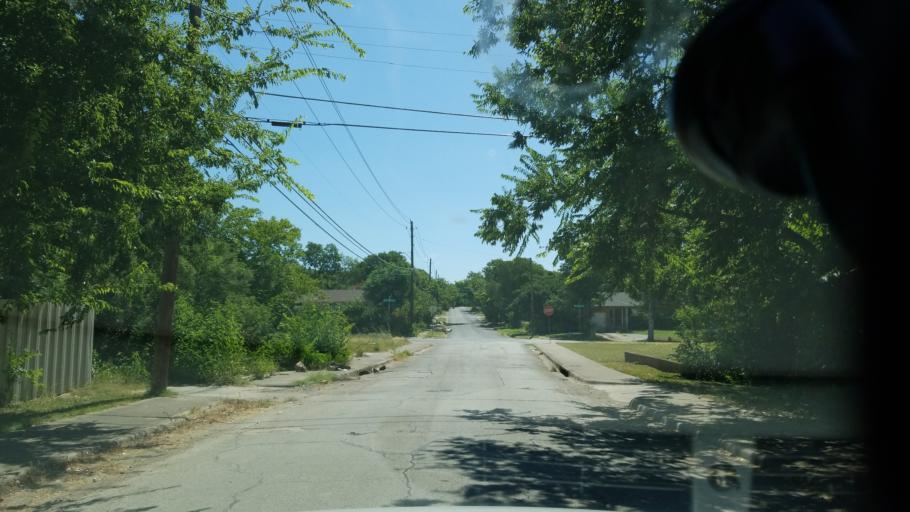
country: US
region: Texas
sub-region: Dallas County
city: Cockrell Hill
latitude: 32.7030
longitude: -96.8179
